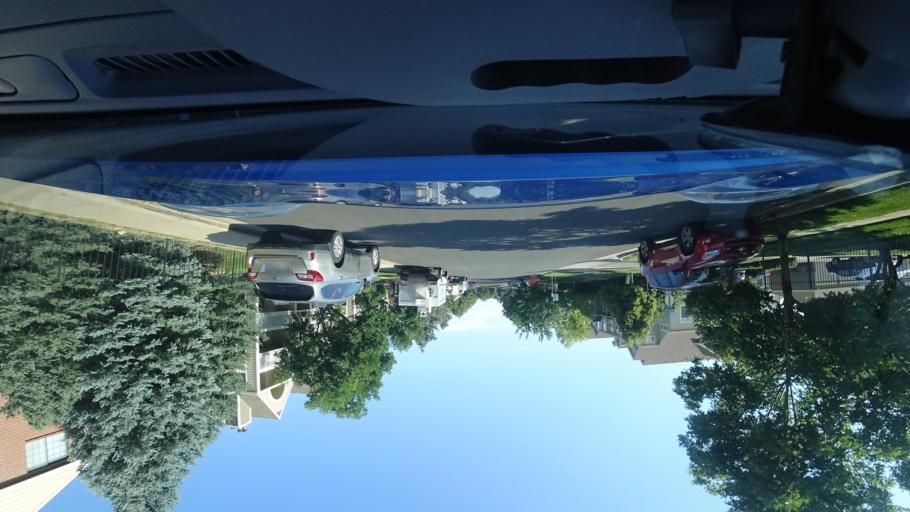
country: US
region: Colorado
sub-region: Adams County
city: Aurora
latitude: 39.6877
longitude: -104.8707
